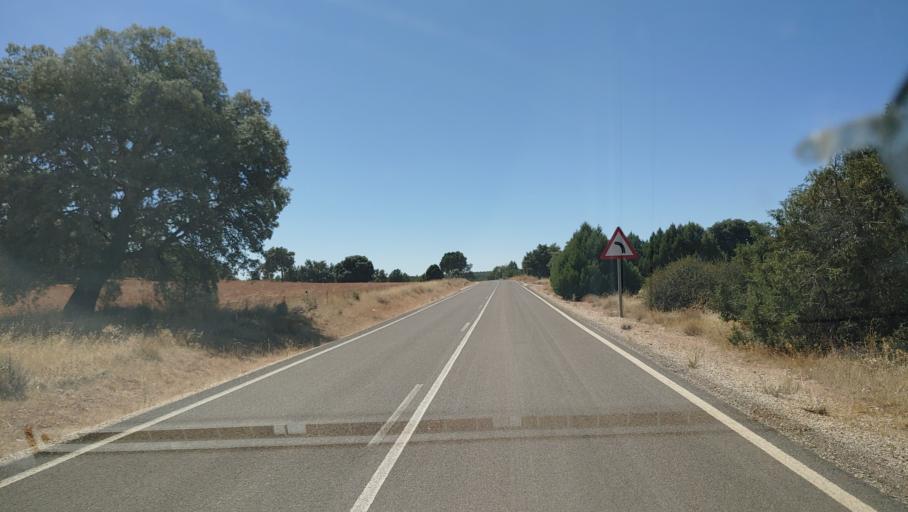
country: ES
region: Castille-La Mancha
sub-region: Provincia de Albacete
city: Ossa de Montiel
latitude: 38.8677
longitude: -2.7955
